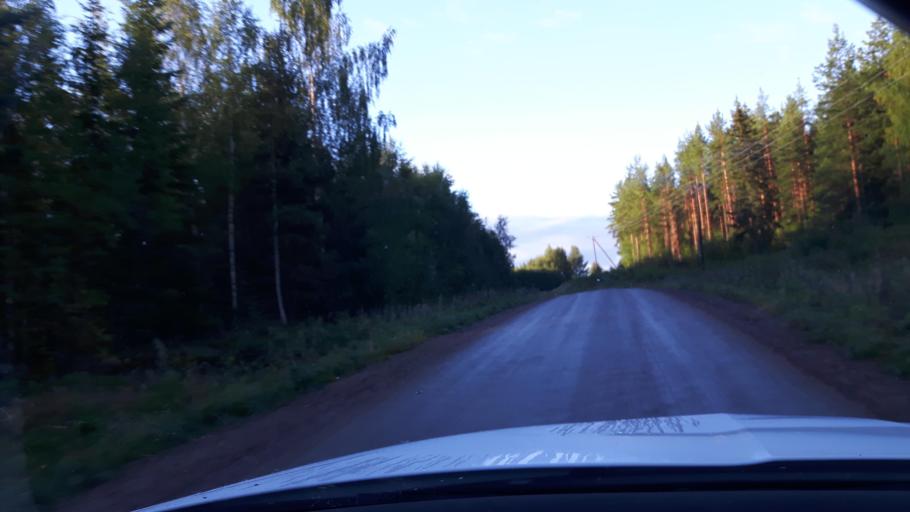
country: SE
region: Vaesternorrland
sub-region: Ange Kommun
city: Ange
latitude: 62.1567
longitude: 15.6626
